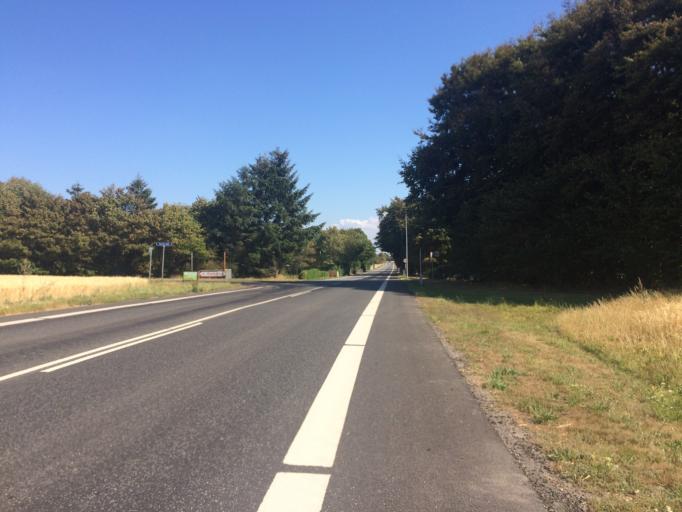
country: DK
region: Central Jutland
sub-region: Holstebro Kommune
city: Vinderup
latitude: 56.5783
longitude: 8.8474
